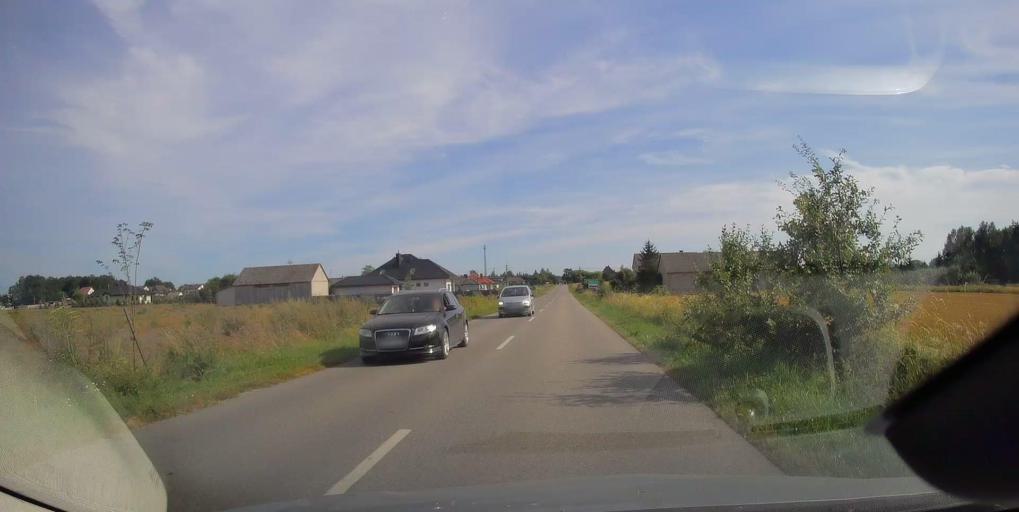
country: PL
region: Lodz Voivodeship
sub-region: Powiat opoczynski
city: Mniszkow
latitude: 51.3787
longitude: 20.0368
